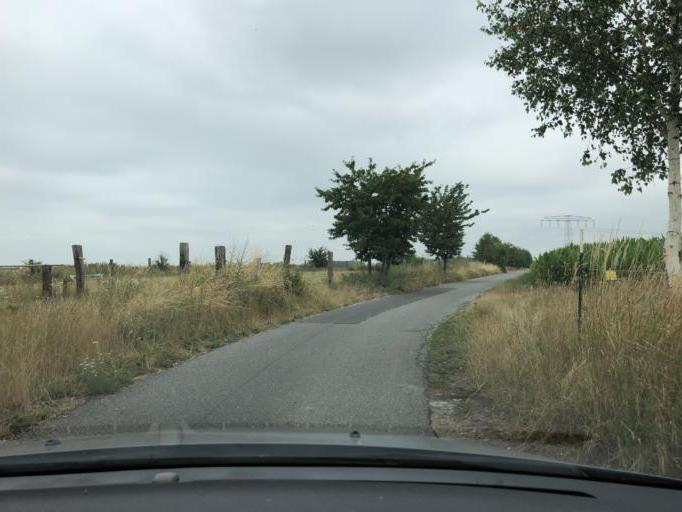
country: DE
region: Saxony
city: Frohburg
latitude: 51.1020
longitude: 12.5610
